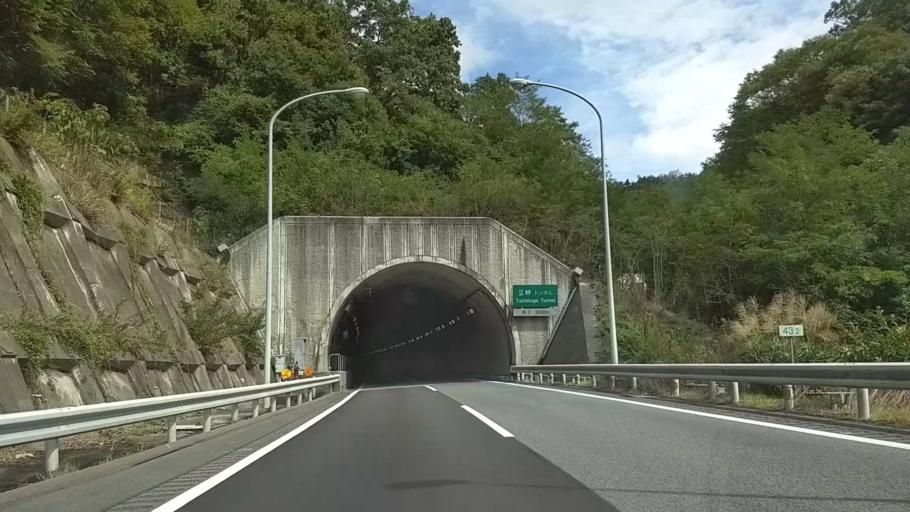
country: JP
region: Nagano
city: Toyoshina
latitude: 36.3594
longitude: 137.9867
